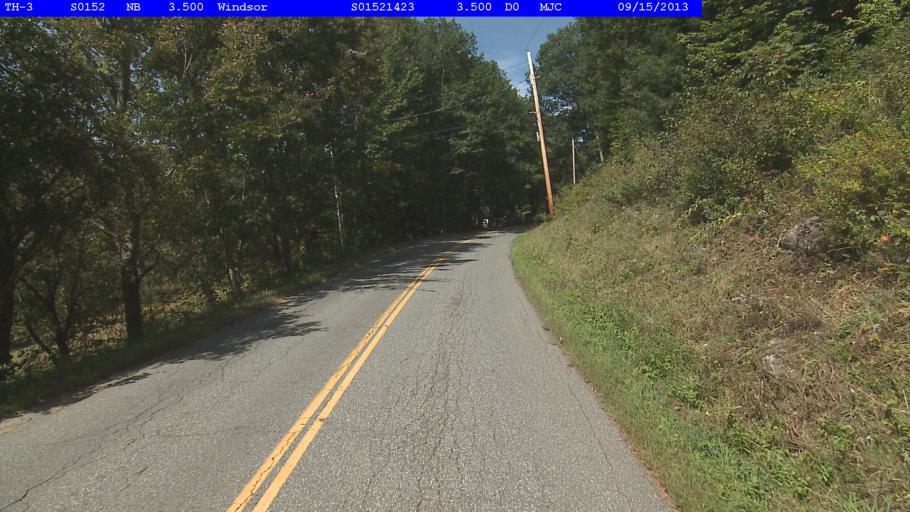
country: US
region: Vermont
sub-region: Windsor County
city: Windsor
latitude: 43.5112
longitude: -72.4342
